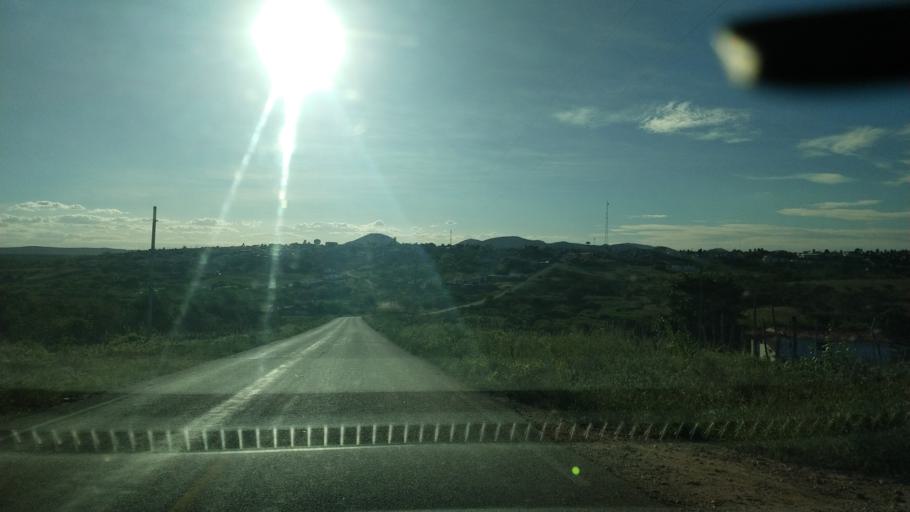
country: BR
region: Rio Grande do Norte
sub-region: Tangara
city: Tangara
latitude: -6.2081
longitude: -35.7936
